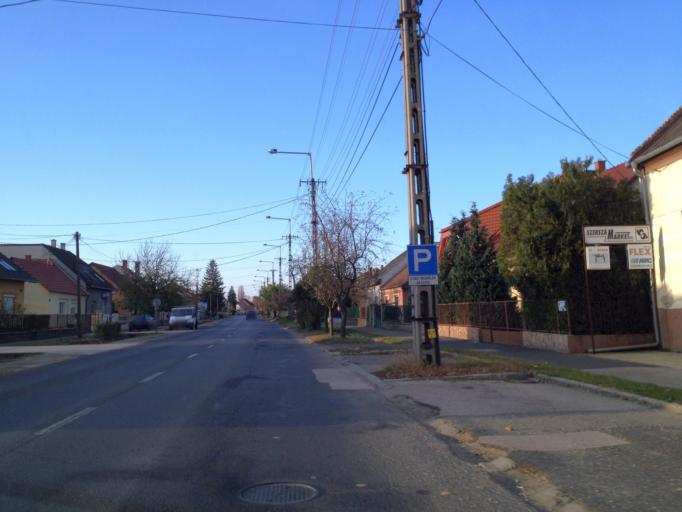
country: HU
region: Gyor-Moson-Sopron
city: Gyor
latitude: 47.6595
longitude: 17.6542
